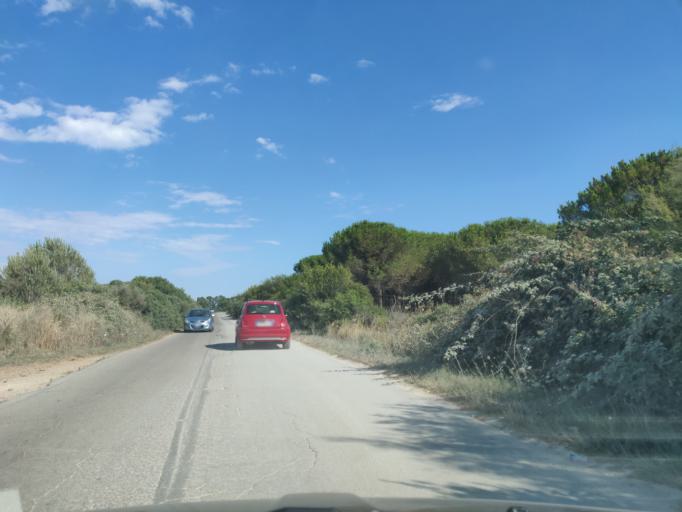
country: IT
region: Latium
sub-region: Citta metropolitana di Roma Capitale
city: Aurelia
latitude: 42.1692
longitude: 11.7413
